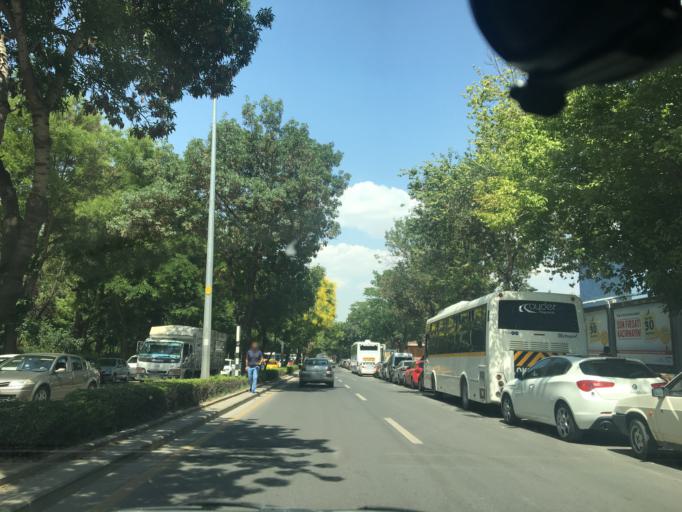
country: TR
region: Ankara
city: Ankara
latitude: 39.9177
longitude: 32.8292
